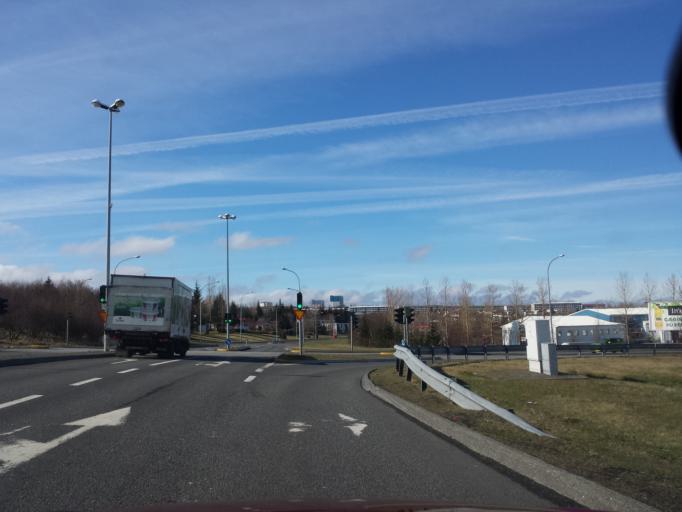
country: IS
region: Capital Region
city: Reykjavik
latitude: 64.1066
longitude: -21.8417
